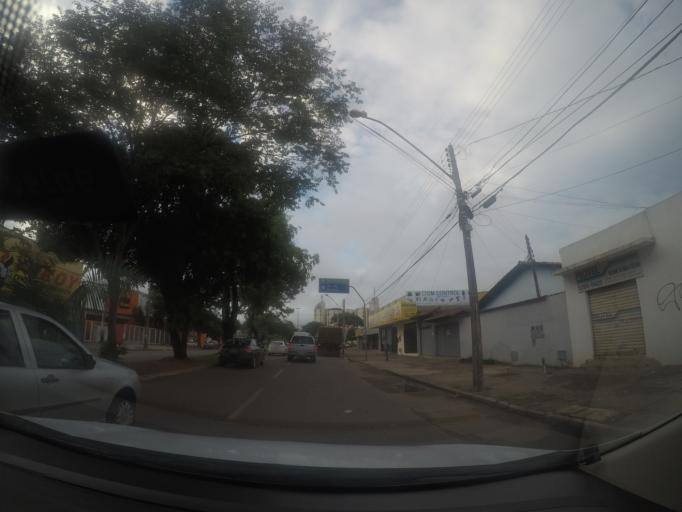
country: BR
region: Goias
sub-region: Goiania
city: Goiania
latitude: -16.6707
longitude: -49.3059
